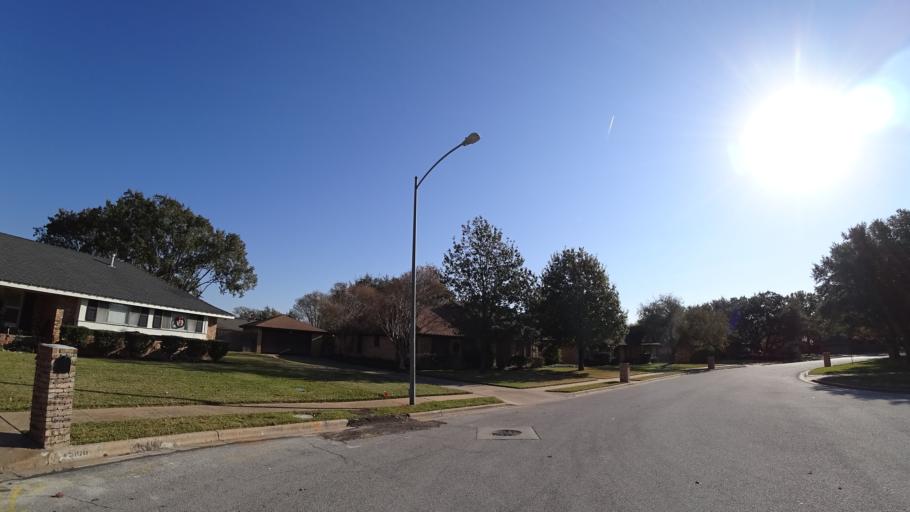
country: US
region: Texas
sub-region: Travis County
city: Shady Hollow
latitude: 30.2209
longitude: -97.8537
